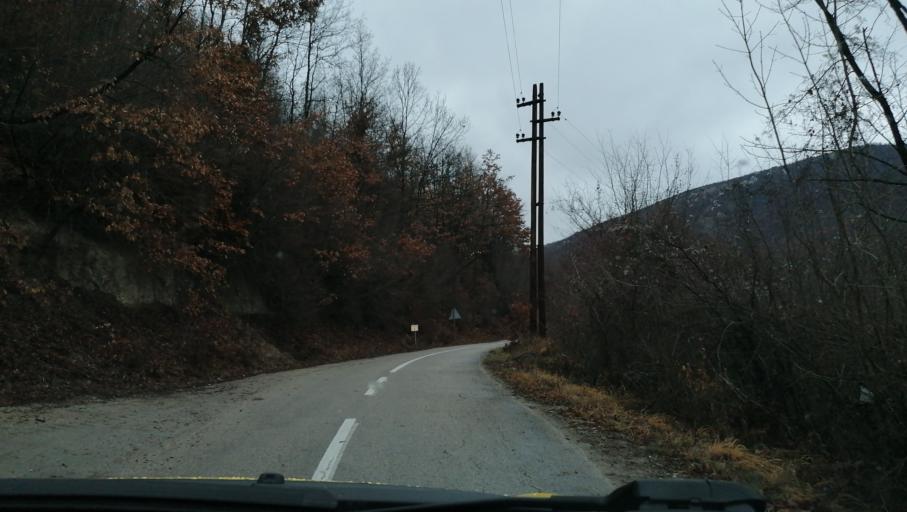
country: RS
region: Central Serbia
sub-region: Pirotski Okrug
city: Dimitrovgrad
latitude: 42.9812
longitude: 22.7835
